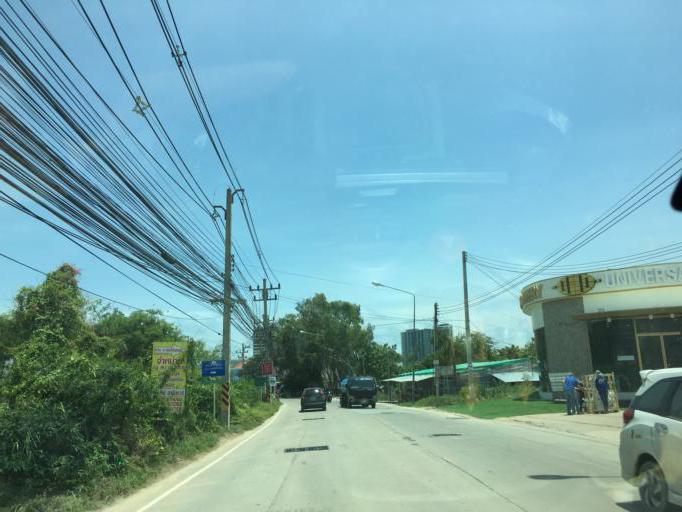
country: TH
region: Chon Buri
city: Phatthaya
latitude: 12.8903
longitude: 100.8898
